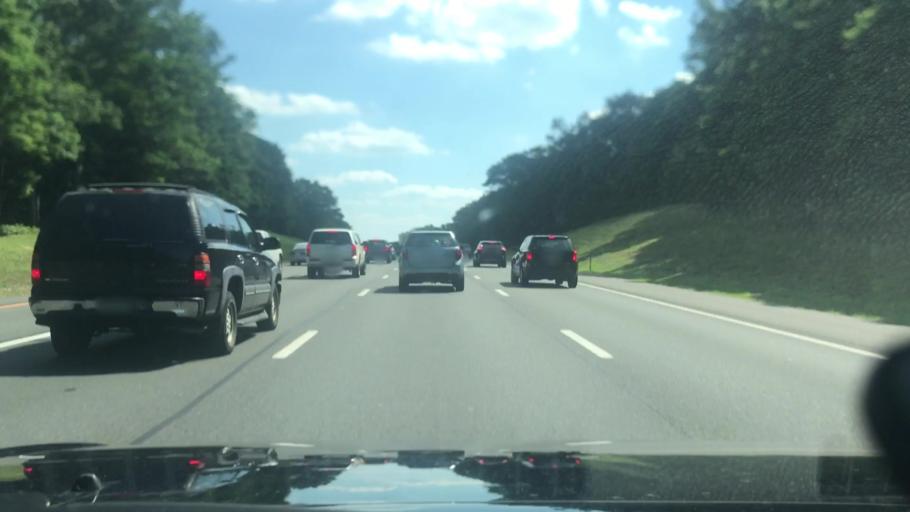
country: US
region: New Jersey
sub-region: Monmouth County
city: Shark River Hills
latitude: 40.2332
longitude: -74.0940
